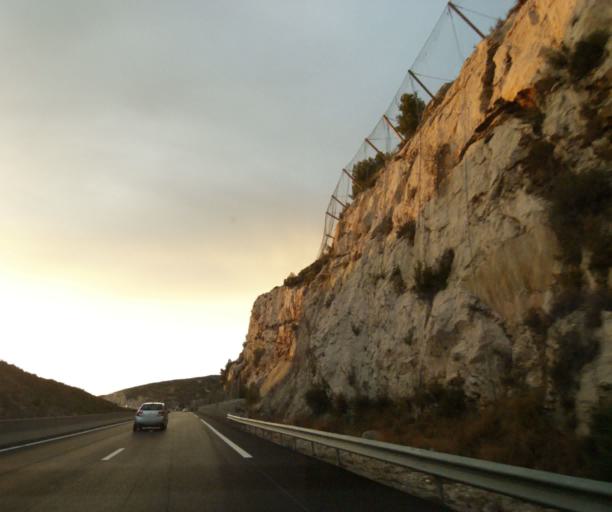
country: FR
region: Provence-Alpes-Cote d'Azur
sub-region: Departement des Bouches-du-Rhone
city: Carry-le-Rouet
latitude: 43.3404
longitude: 5.1527
